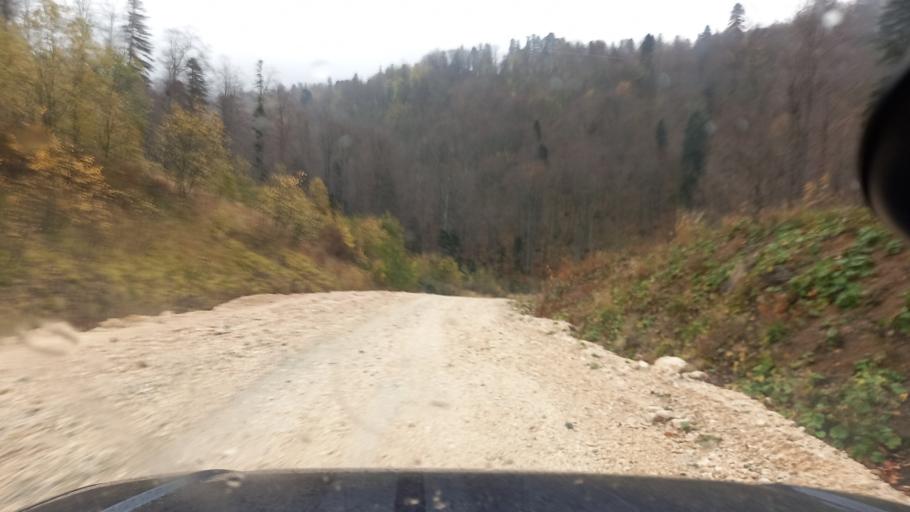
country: RU
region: Krasnodarskiy
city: Dagomys
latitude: 43.9848
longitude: 39.8506
